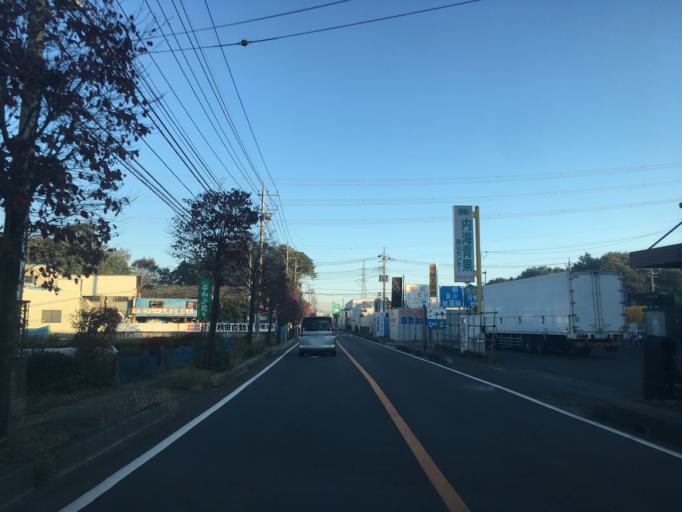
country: JP
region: Saitama
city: Tokorozawa
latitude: 35.8397
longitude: 139.4664
